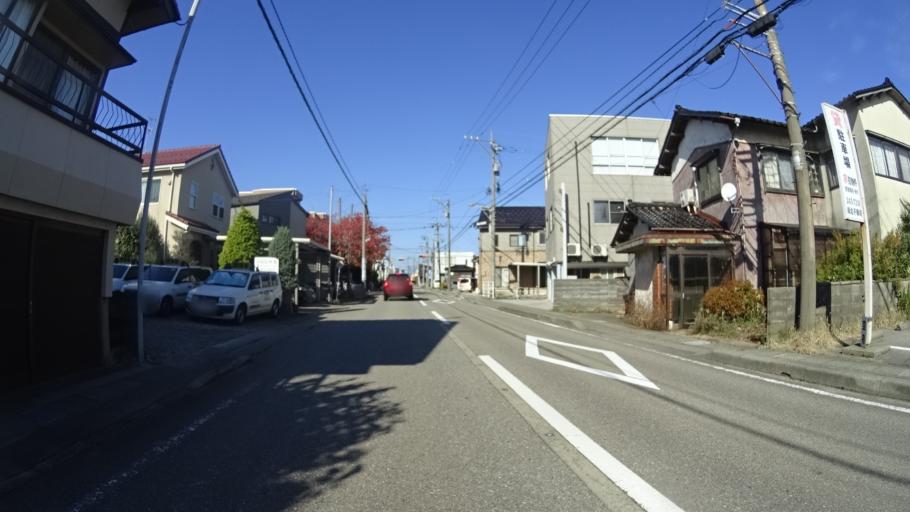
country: JP
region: Ishikawa
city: Kanazawa-shi
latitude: 36.5952
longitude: 136.6096
